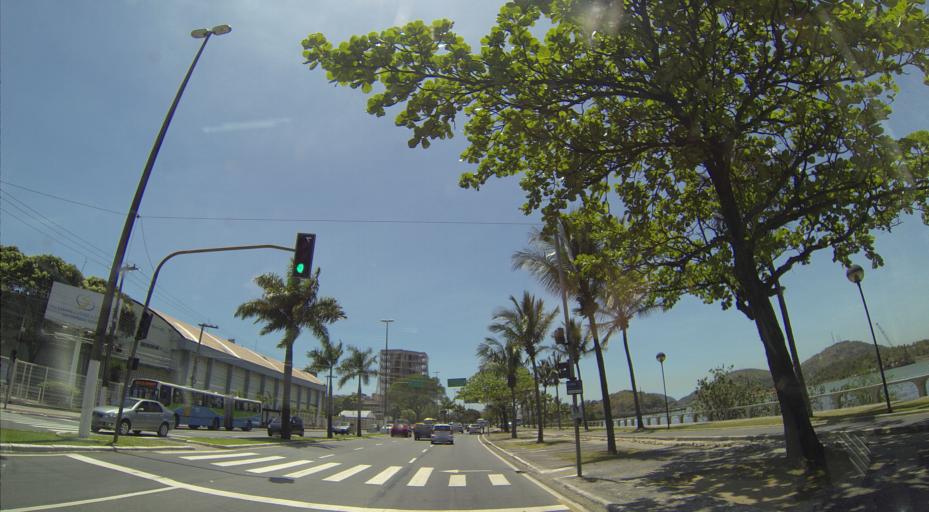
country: BR
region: Espirito Santo
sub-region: Vitoria
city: Vitoria
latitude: -20.3184
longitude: -40.3220
